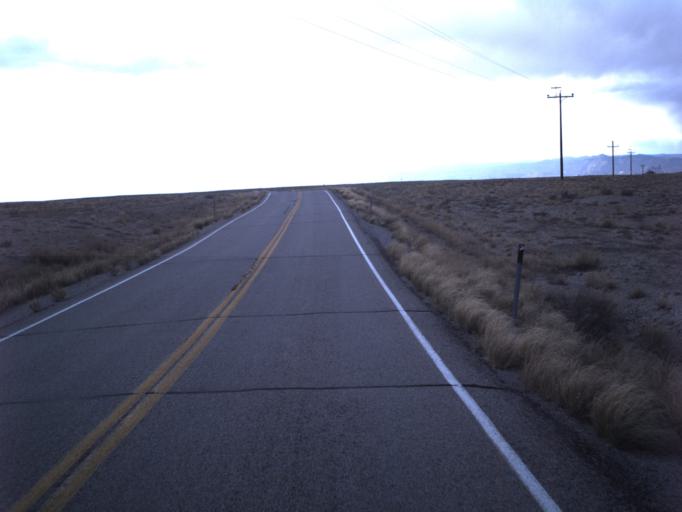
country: US
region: Utah
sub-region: Grand County
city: Moab
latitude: 38.9023
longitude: -109.3161
